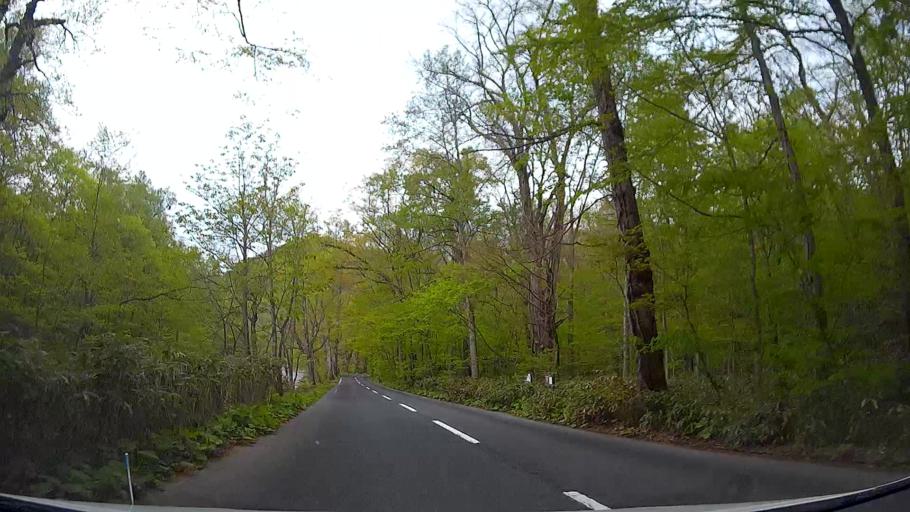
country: JP
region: Aomori
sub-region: Aomori Shi
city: Furudate
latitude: 40.5675
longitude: 140.9767
